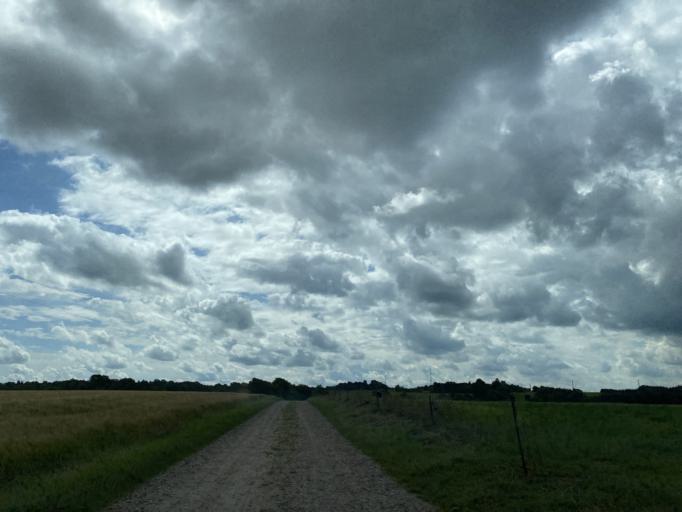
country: DK
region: Central Jutland
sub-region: Silkeborg Kommune
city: Silkeborg
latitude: 56.2192
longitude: 9.5684
